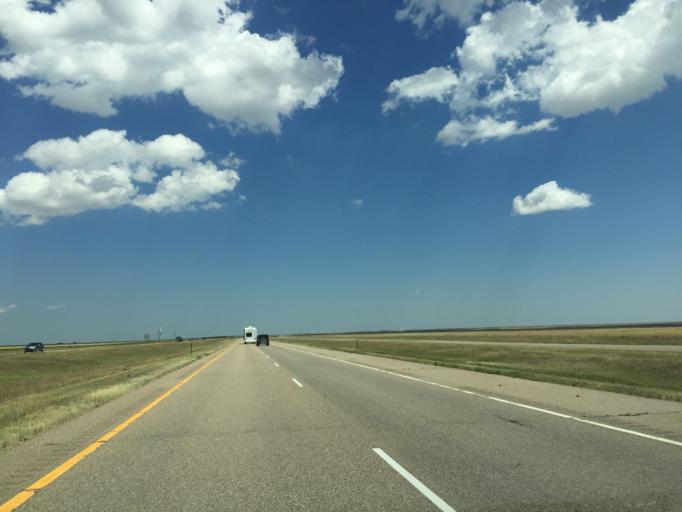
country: US
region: Colorado
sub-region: Lincoln County
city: Hugo
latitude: 39.2768
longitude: -103.4724
